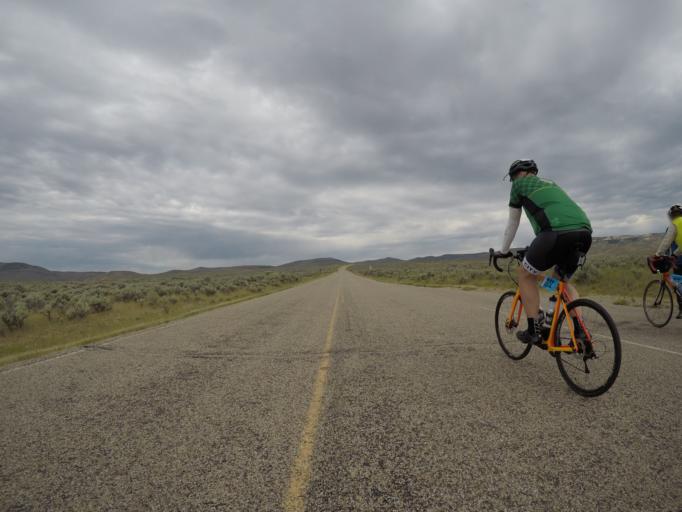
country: US
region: Wyoming
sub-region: Lincoln County
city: Kemmerer
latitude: 41.8248
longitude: -110.7636
